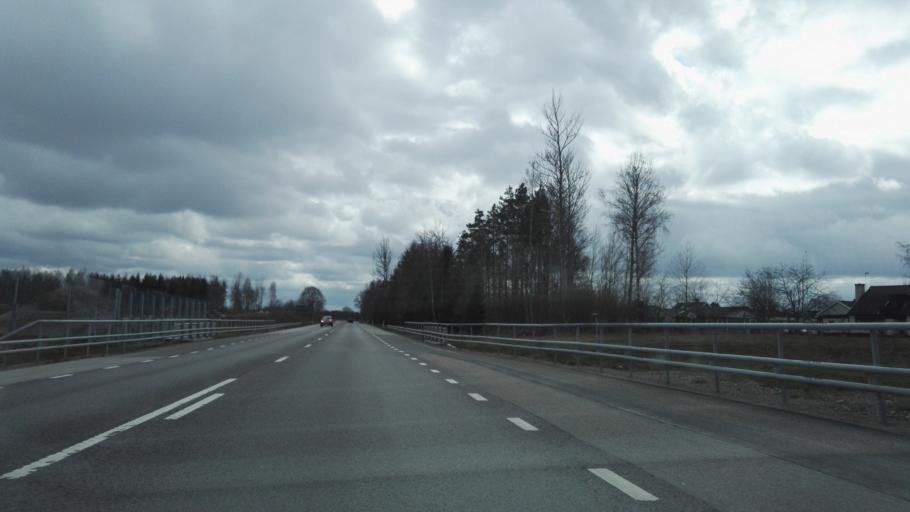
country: SE
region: Kronoberg
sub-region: Vaxjo Kommun
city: Vaexjoe
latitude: 56.8767
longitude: 14.7431
